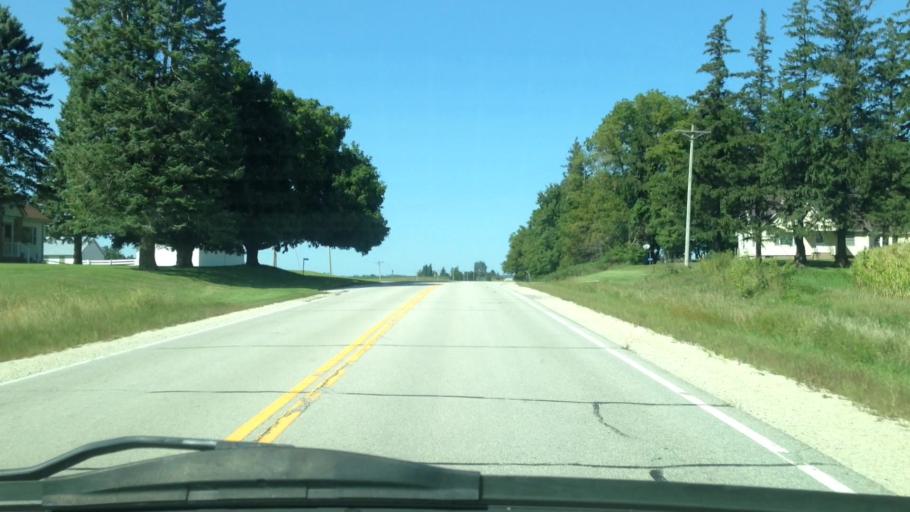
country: US
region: Minnesota
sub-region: Houston County
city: Spring Grove
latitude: 43.6071
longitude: -91.7902
